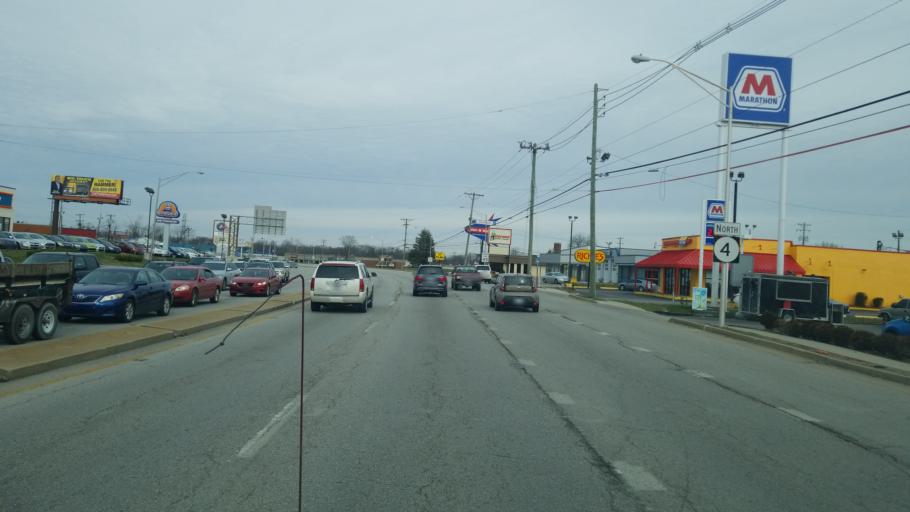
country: US
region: Kentucky
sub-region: Fayette County
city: Lexington-Fayette
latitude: 38.0462
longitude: -84.4539
